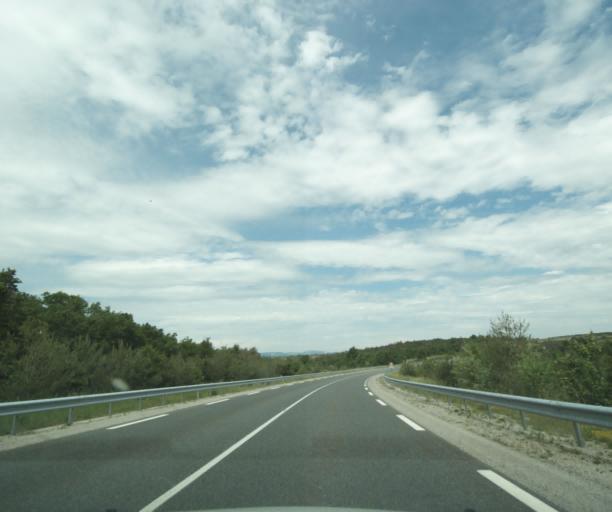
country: FR
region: Midi-Pyrenees
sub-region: Departement de l'Aveyron
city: Creissels
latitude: 44.0230
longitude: 3.0631
